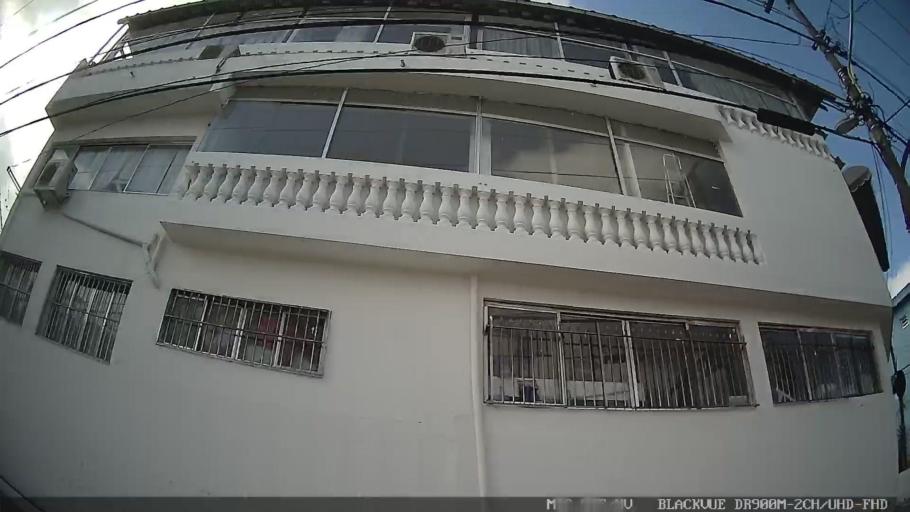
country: BR
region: Sao Paulo
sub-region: Guarulhos
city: Guarulhos
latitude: -23.5388
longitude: -46.4812
